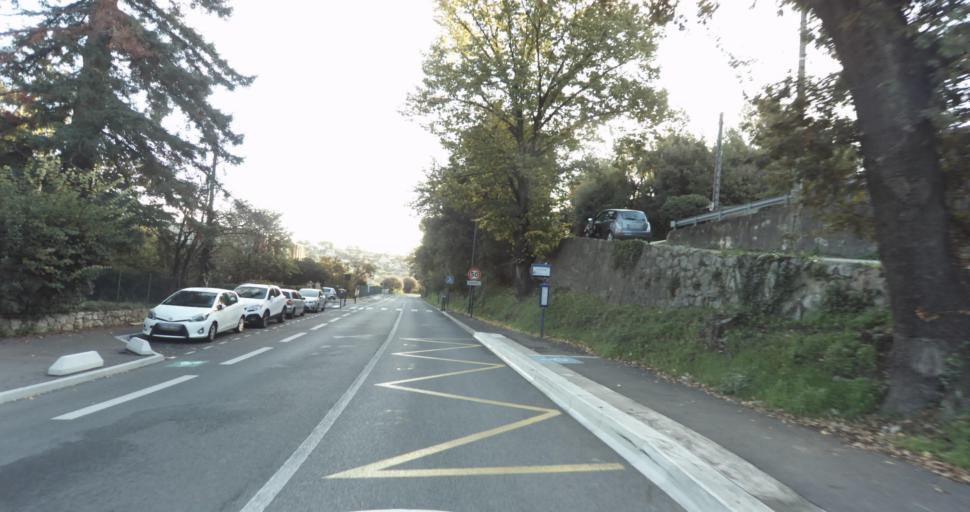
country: FR
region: Provence-Alpes-Cote d'Azur
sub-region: Departement des Alpes-Maritimes
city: Vence
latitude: 43.7155
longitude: 7.1231
